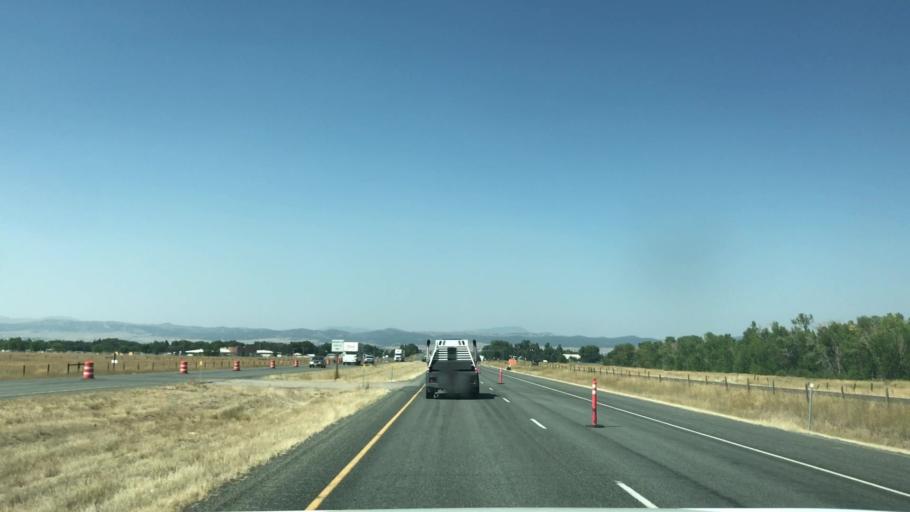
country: US
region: Montana
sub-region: Lewis and Clark County
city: Helena Valley West Central
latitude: 46.6526
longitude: -112.0113
